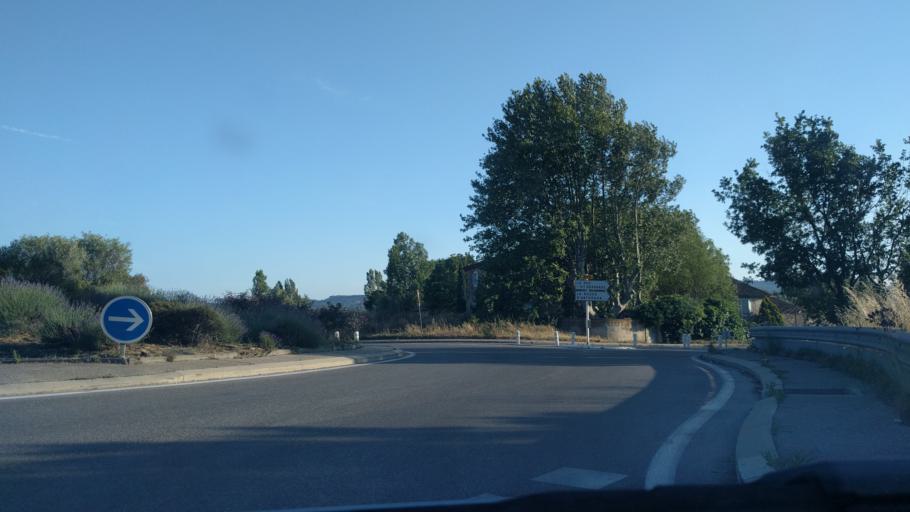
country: FR
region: Provence-Alpes-Cote d'Azur
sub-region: Departement du Vaucluse
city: Pertuis
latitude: 43.6604
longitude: 5.4948
